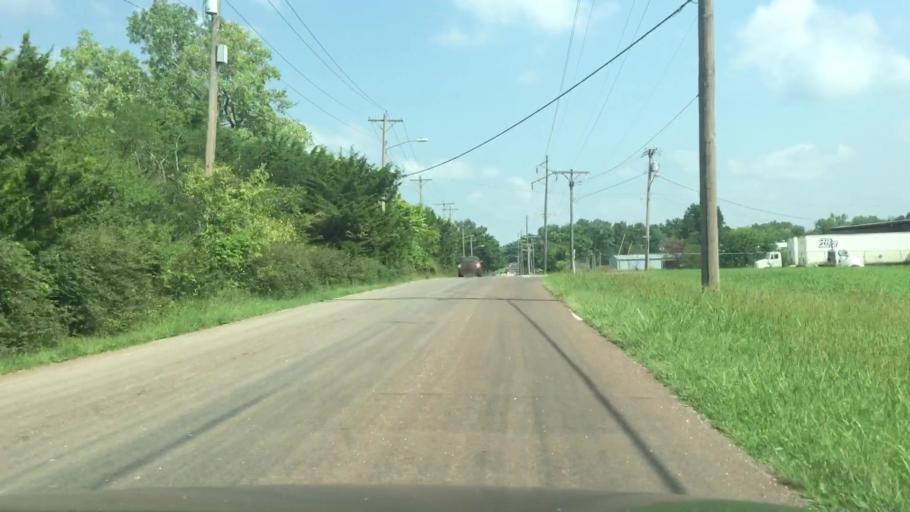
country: US
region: Kansas
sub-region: Allen County
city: Iola
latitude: 37.9071
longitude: -95.4056
